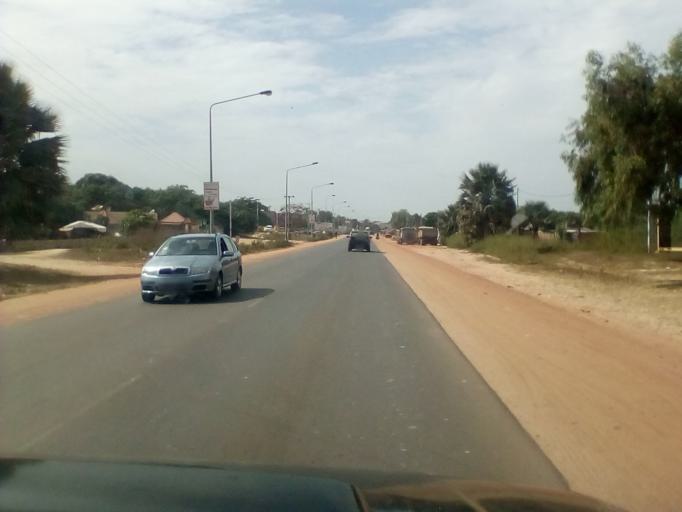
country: GM
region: Western
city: Sukuta
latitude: 13.3979
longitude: -16.7084
